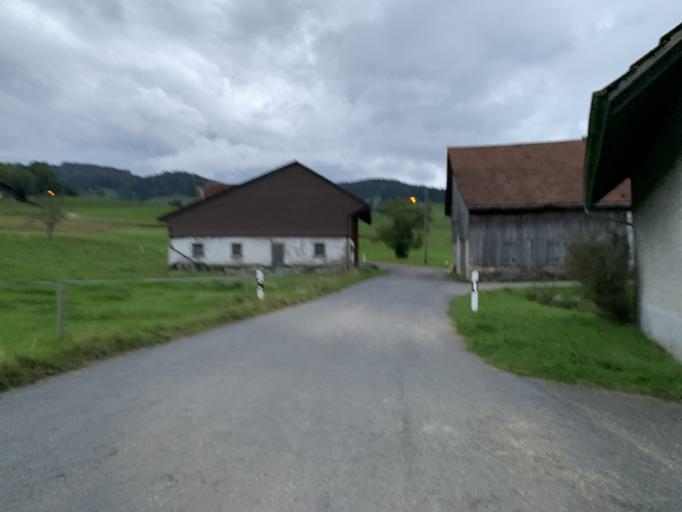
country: CH
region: Zurich
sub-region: Bezirk Hinwil
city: Hadlikon
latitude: 47.3064
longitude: 8.8658
